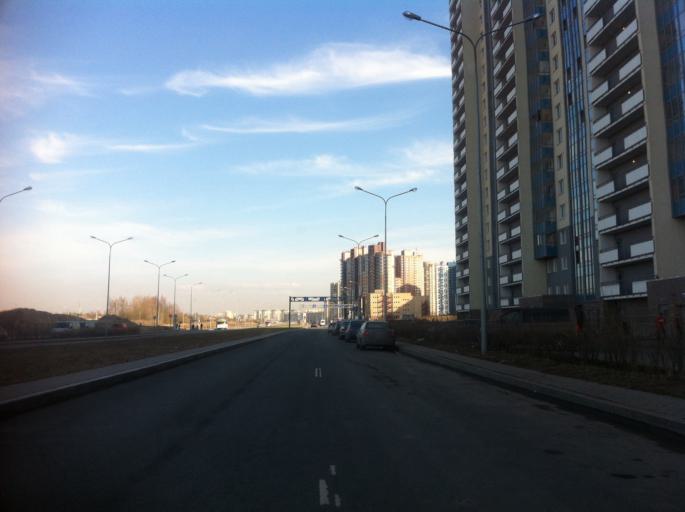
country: RU
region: St.-Petersburg
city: Uritsk
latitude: 59.8662
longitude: 30.1790
